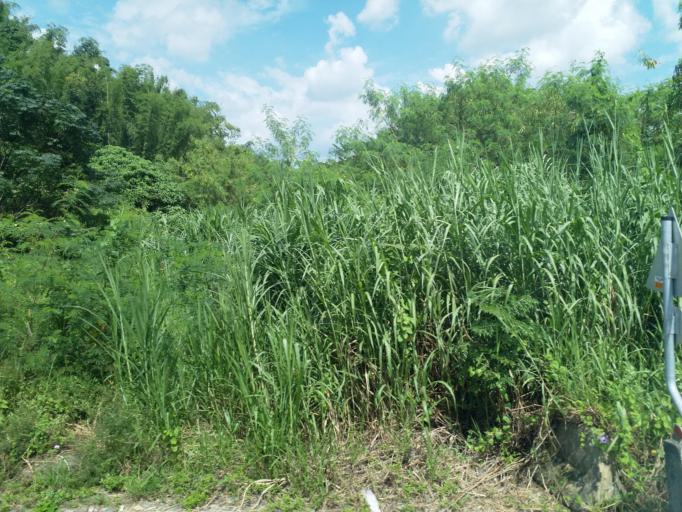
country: TW
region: Taiwan
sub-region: Pingtung
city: Pingtung
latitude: 22.8797
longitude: 120.5681
